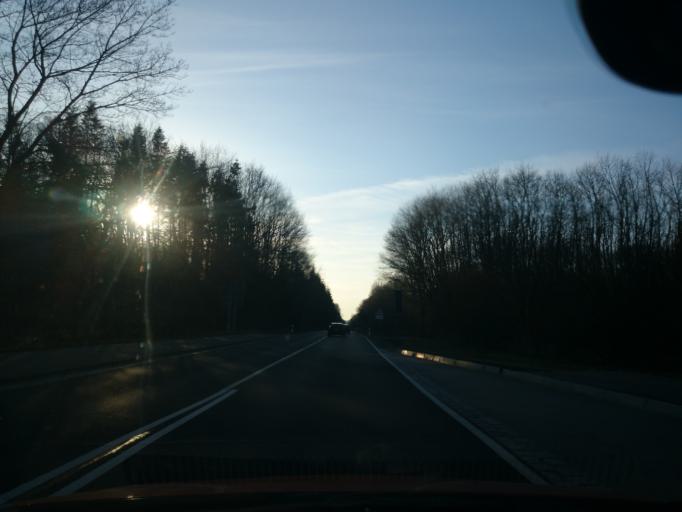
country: DE
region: Mecklenburg-Vorpommern
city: Velgast
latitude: 54.2992
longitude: 12.8612
